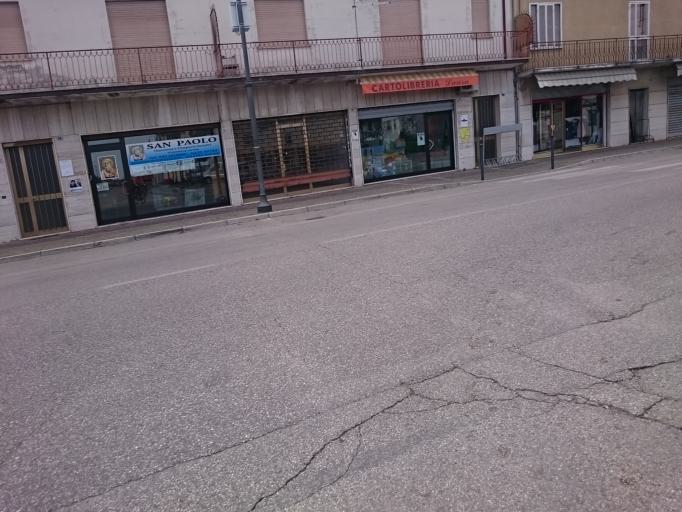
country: IT
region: Veneto
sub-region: Provincia di Padova
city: Ponso
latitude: 45.1919
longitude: 11.5863
